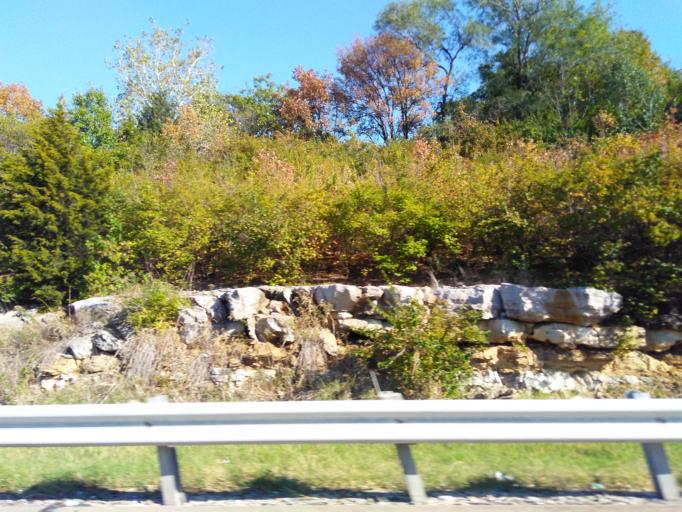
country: US
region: Missouri
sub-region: Saint Louis County
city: Concord
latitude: 38.5101
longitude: -90.3596
